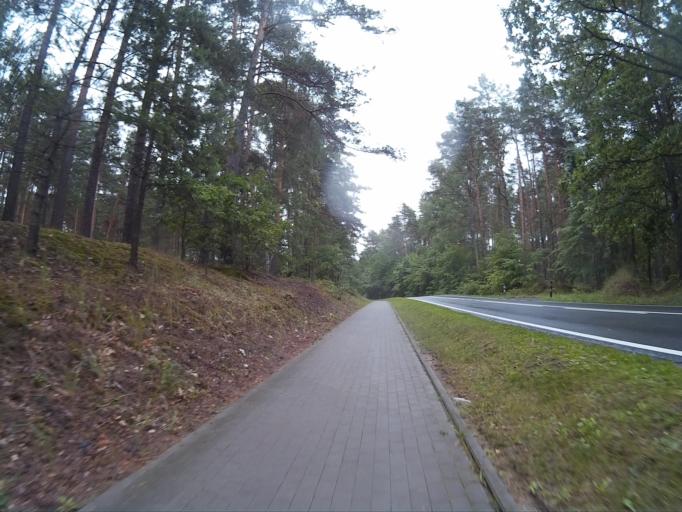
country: PL
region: Kujawsko-Pomorskie
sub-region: Powiat swiecki
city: Osie
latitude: 53.6102
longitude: 18.3011
